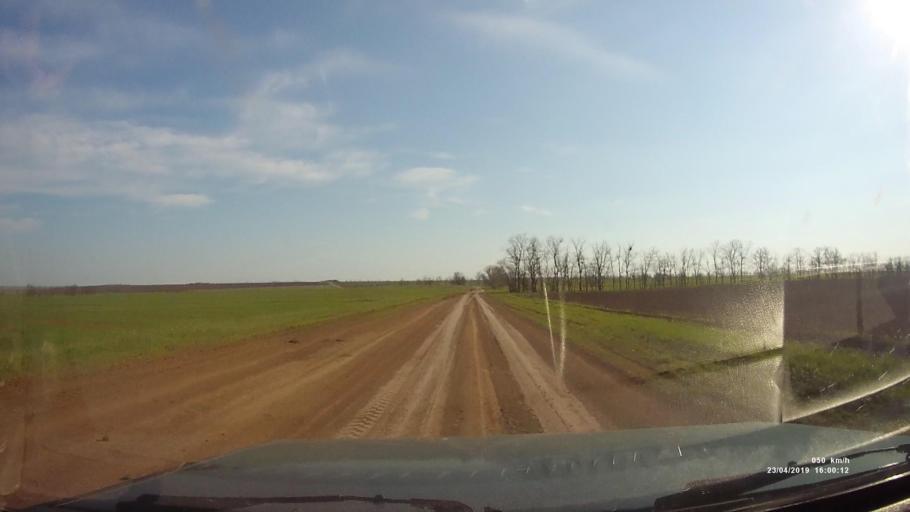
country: RU
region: Rostov
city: Remontnoye
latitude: 46.5110
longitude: 43.1082
